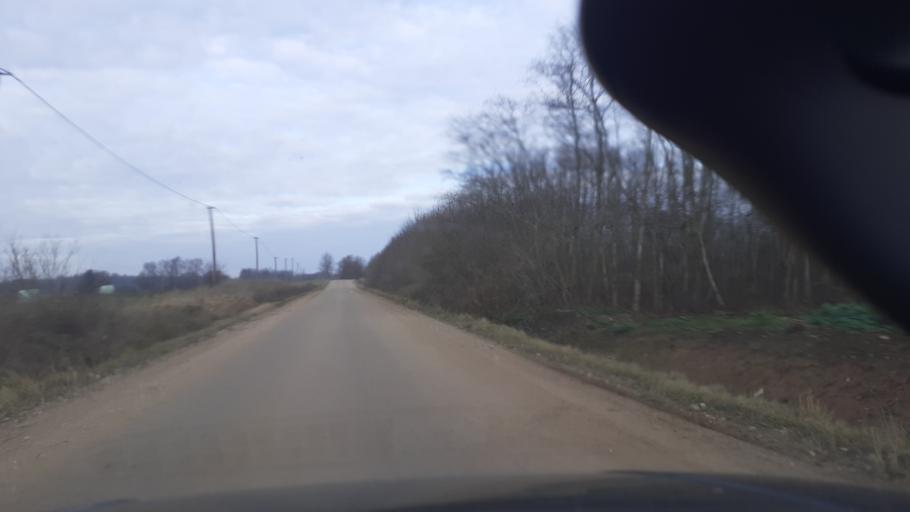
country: LV
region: Alsunga
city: Alsunga
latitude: 56.9050
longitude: 21.6549
